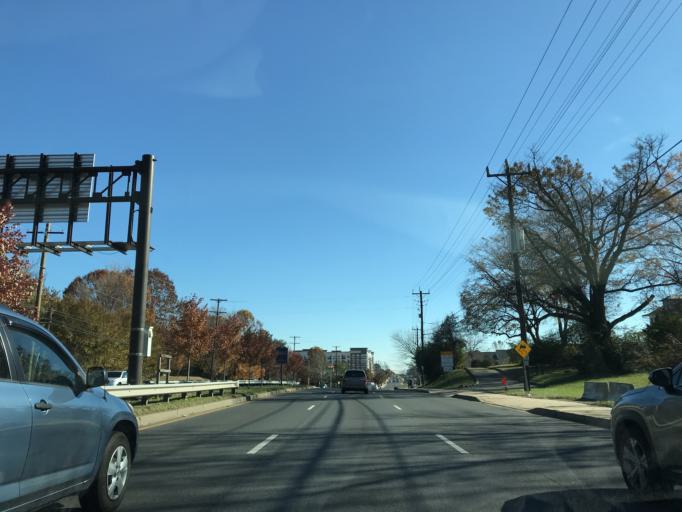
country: US
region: Maryland
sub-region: Montgomery County
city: Derwood
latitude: 39.1201
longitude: -77.1738
